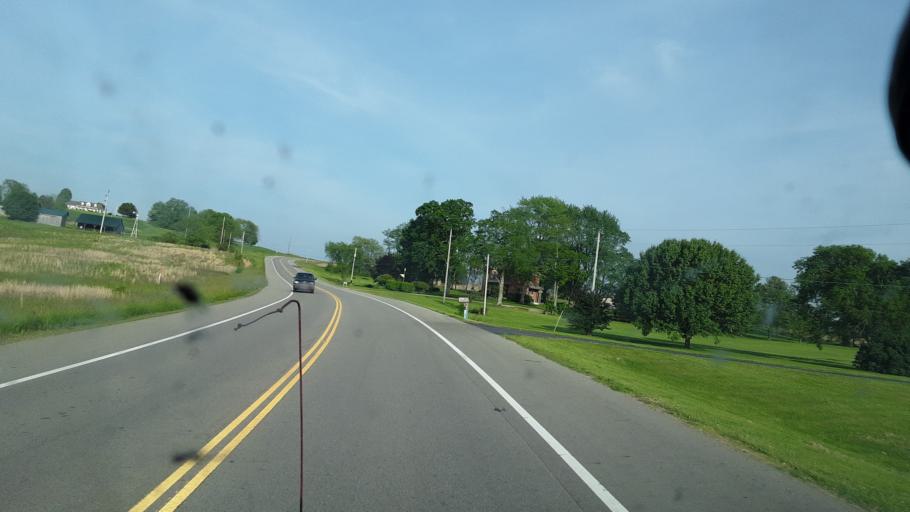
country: US
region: Ohio
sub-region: Ross County
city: Kingston
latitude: 39.5268
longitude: -82.8344
